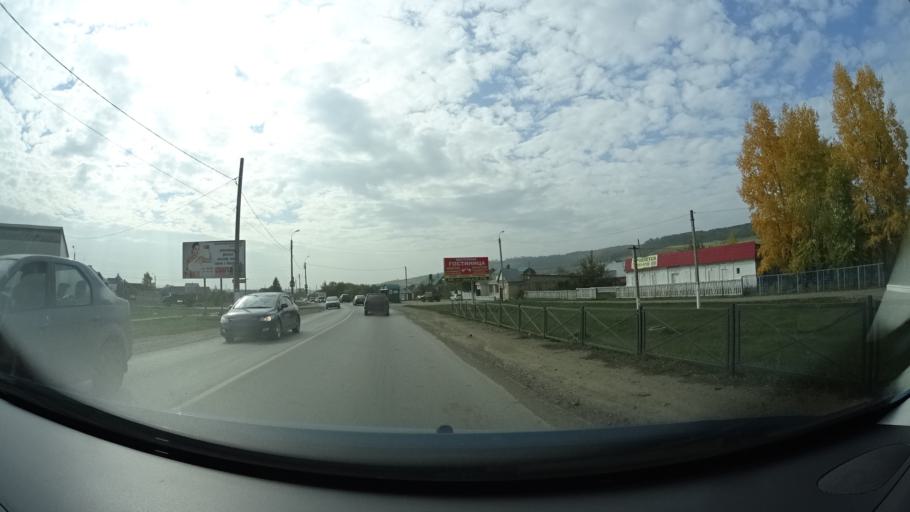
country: RU
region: Bashkortostan
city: Oktyabr'skiy
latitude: 54.5128
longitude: 53.5196
